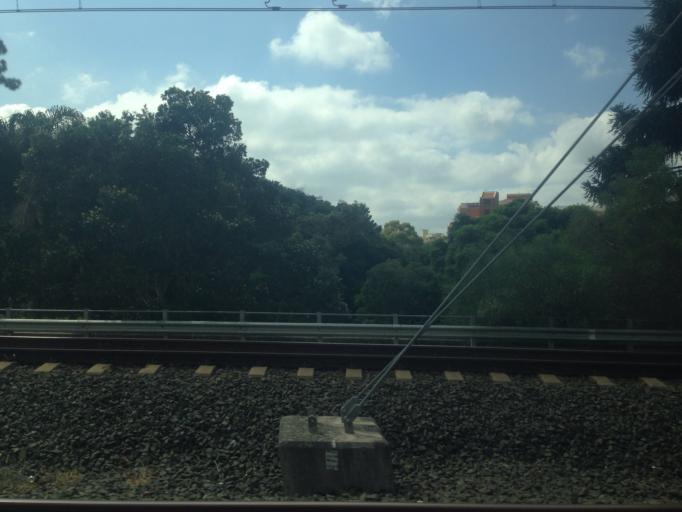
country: AU
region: New South Wales
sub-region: Willoughby
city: Chatswood
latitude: -33.7992
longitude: 151.1810
